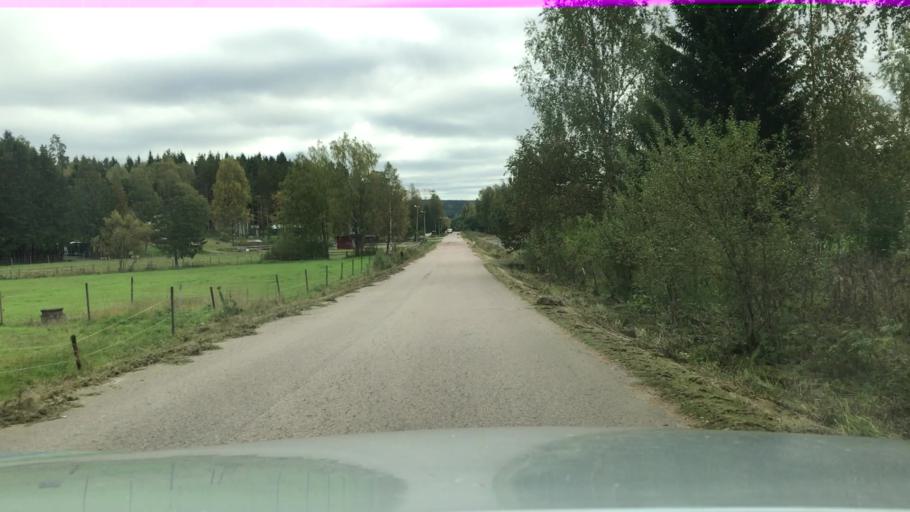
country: SE
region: Vaermland
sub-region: Munkfors Kommun
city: Munkfors
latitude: 59.8393
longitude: 13.5024
